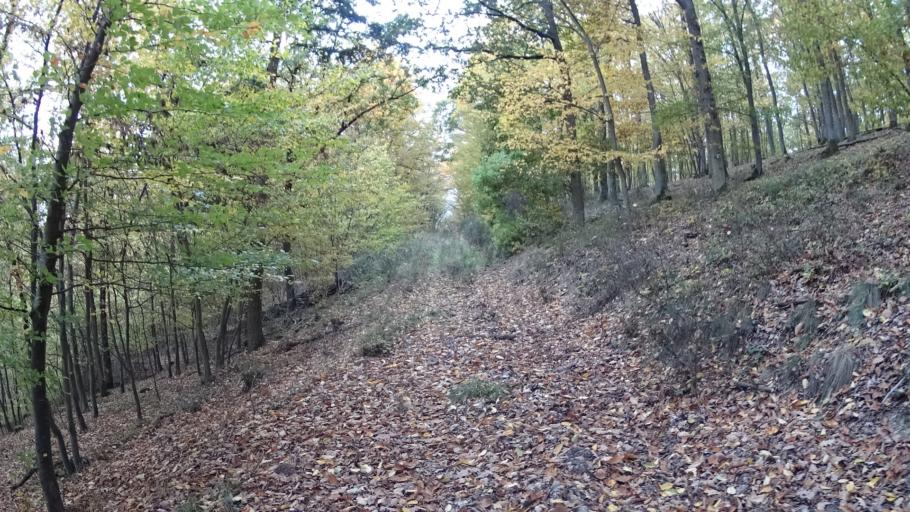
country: DE
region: Rheinland-Pfalz
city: Kalkofen
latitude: 49.7468
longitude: 7.8355
